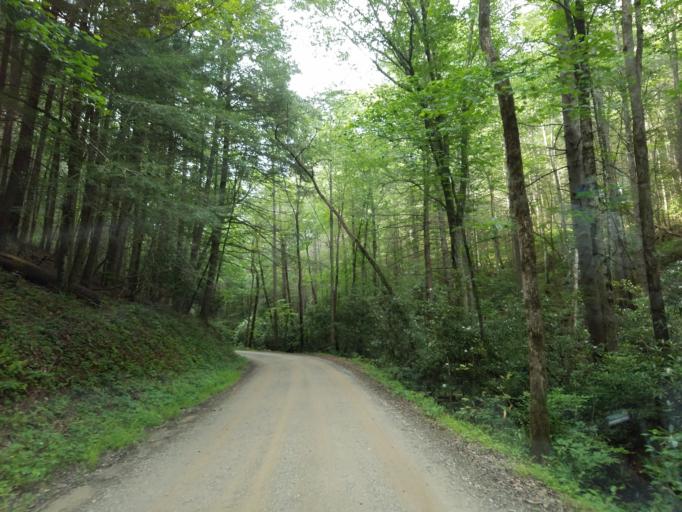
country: US
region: Georgia
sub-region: Union County
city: Blairsville
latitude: 34.7676
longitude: -84.0676
